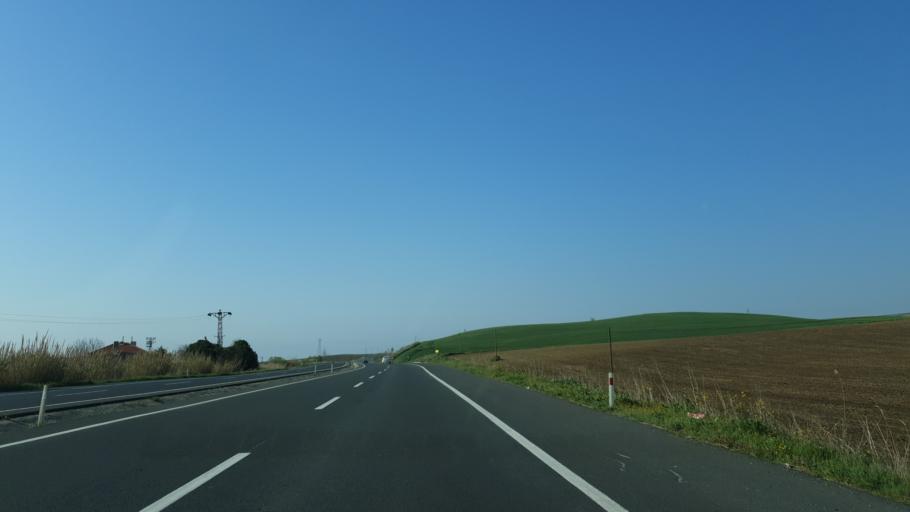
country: TR
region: Tekirdag
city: Corlu
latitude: 41.0425
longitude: 27.7319
